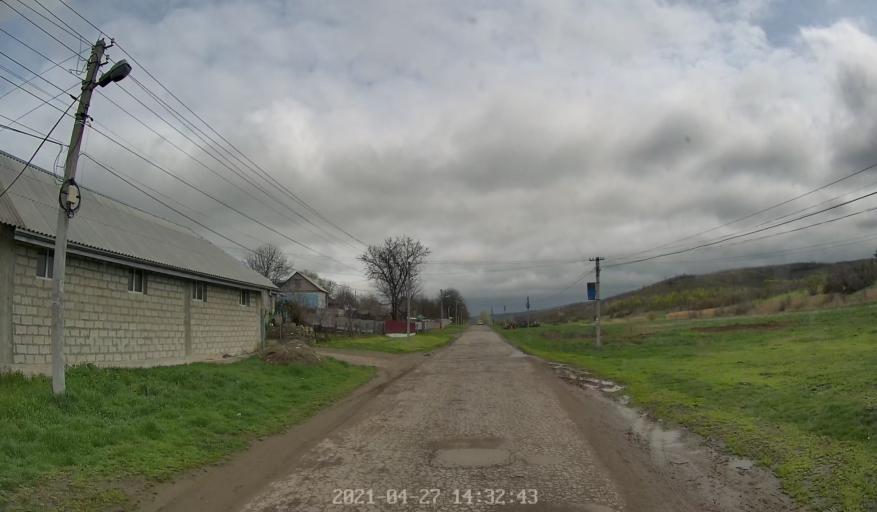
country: MD
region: Chisinau
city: Vadul lui Voda
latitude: 47.0622
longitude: 29.0146
